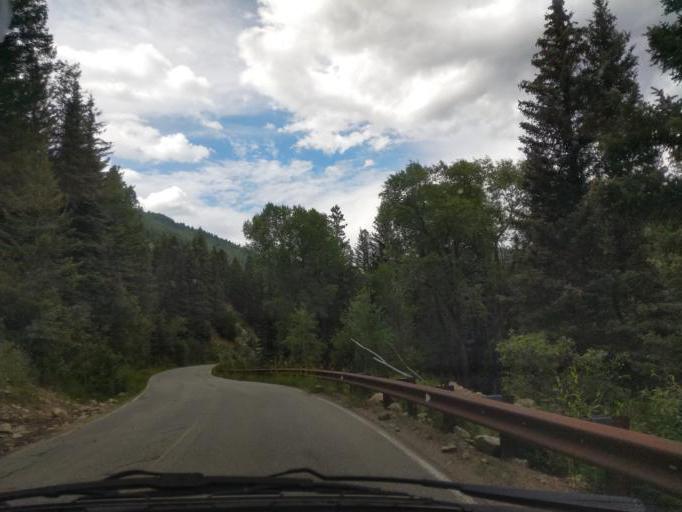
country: US
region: Colorado
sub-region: Garfield County
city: Carbondale
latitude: 39.1070
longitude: -107.2651
